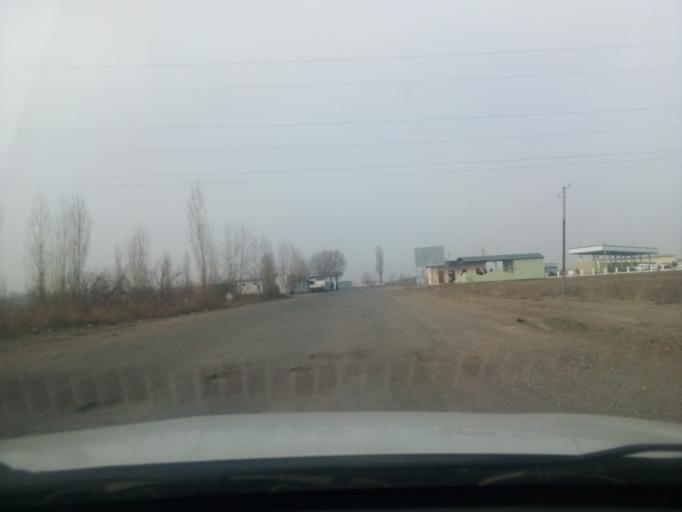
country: UZ
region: Namangan
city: Pop Shahri
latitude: 40.9079
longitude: 71.1023
